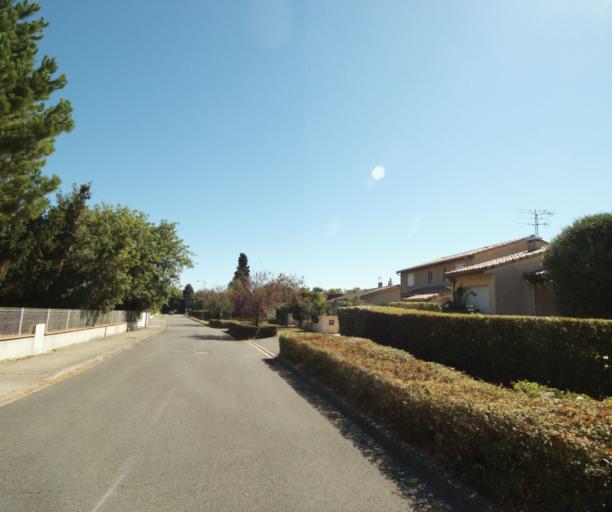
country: FR
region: Midi-Pyrenees
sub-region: Departement de la Haute-Garonne
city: Castanet-Tolosan
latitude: 43.5225
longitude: 1.5009
